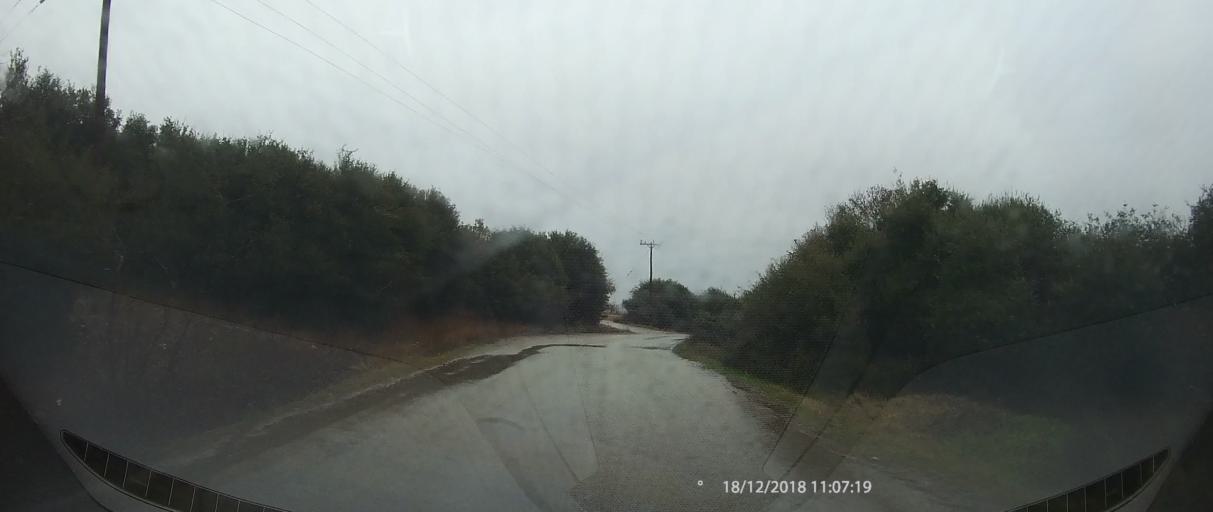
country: GR
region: Central Macedonia
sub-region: Nomos Pierias
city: Kato Milia
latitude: 40.2251
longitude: 22.3337
